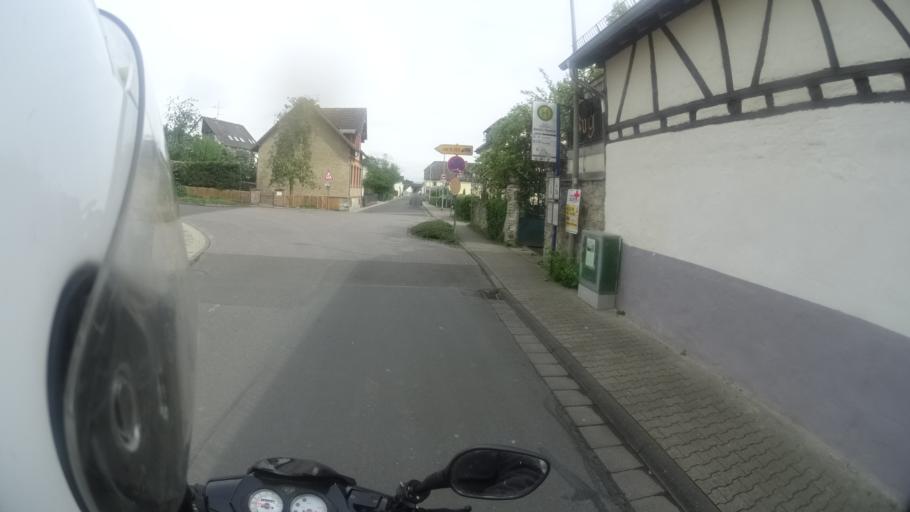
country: DE
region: Hesse
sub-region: Regierungsbezirk Darmstadt
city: Walluf
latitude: 50.0368
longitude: 8.1557
